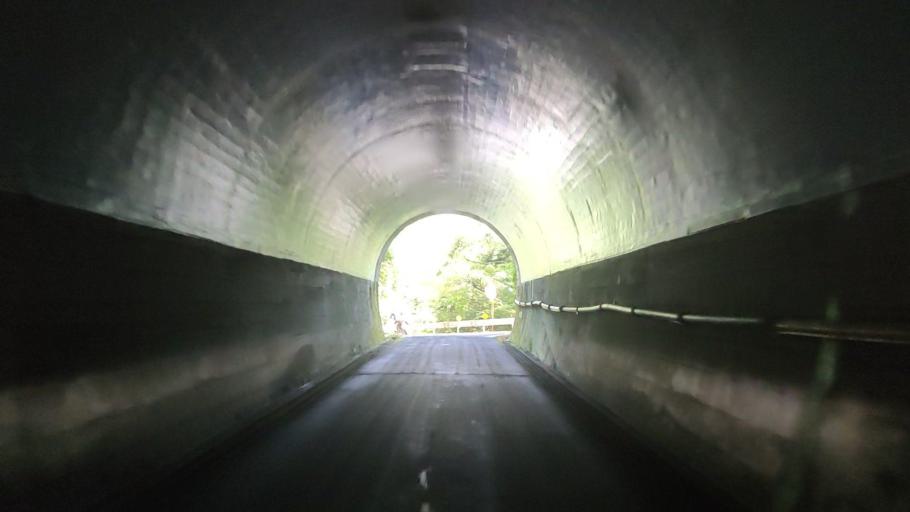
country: JP
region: Wakayama
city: Shingu
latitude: 33.9375
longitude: 135.9271
